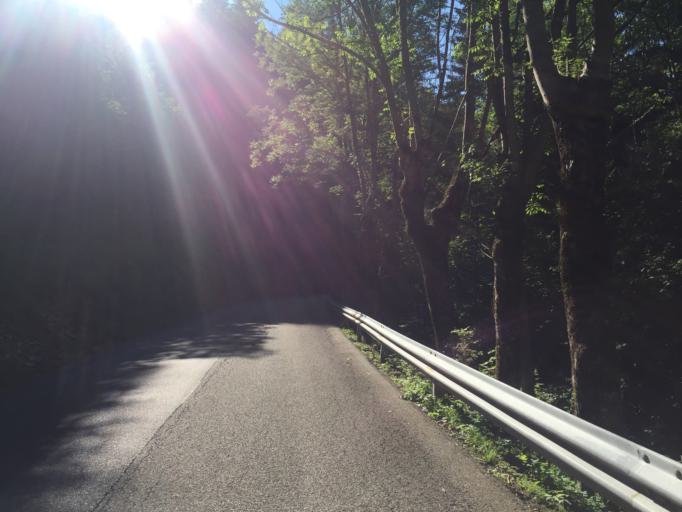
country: IT
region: Friuli Venezia Giulia
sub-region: Provincia di Udine
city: Forni Avoltri
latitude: 46.5786
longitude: 12.8038
